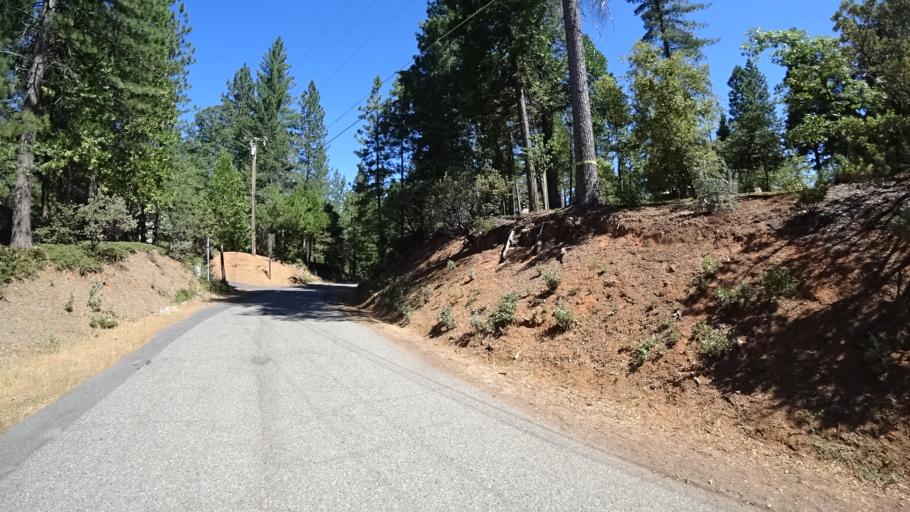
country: US
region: California
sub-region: Calaveras County
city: Arnold
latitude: 38.2410
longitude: -120.3378
